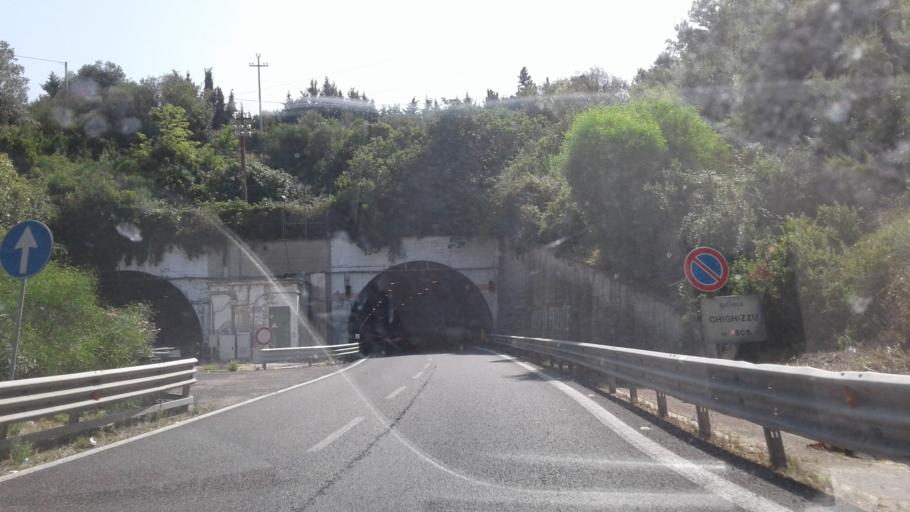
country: IT
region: Sardinia
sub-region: Provincia di Sassari
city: Tissi
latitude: 40.6978
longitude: 8.5682
